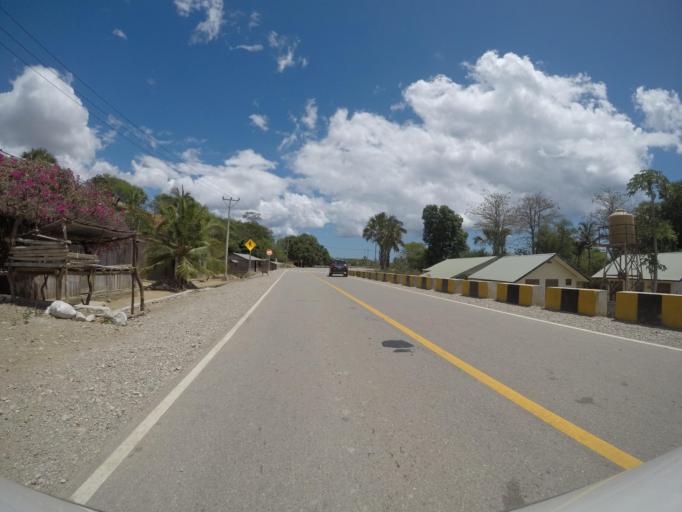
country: TL
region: Lautem
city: Lospalos
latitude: -8.4110
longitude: 126.7382
